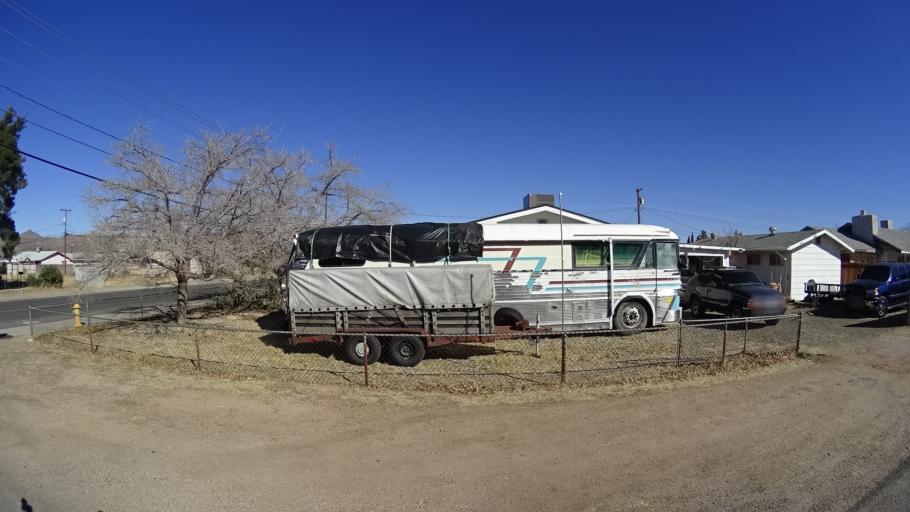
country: US
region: Arizona
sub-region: Mohave County
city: Kingman
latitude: 35.2068
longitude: -114.0289
